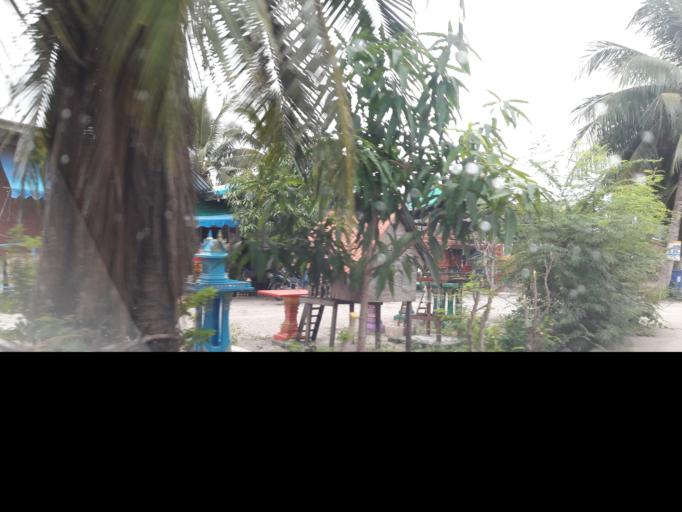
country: TH
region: Ratchaburi
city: Damnoen Saduak
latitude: 13.5974
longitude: 99.9037
